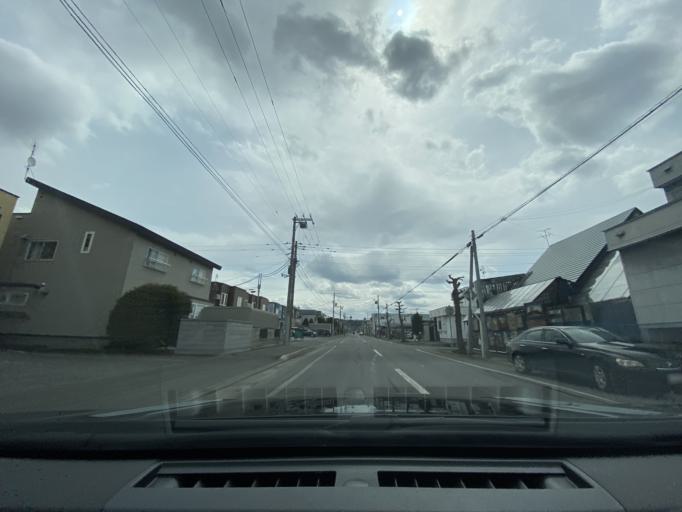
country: JP
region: Hokkaido
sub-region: Asahikawa-shi
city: Asahikawa
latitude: 43.7609
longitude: 142.3538
